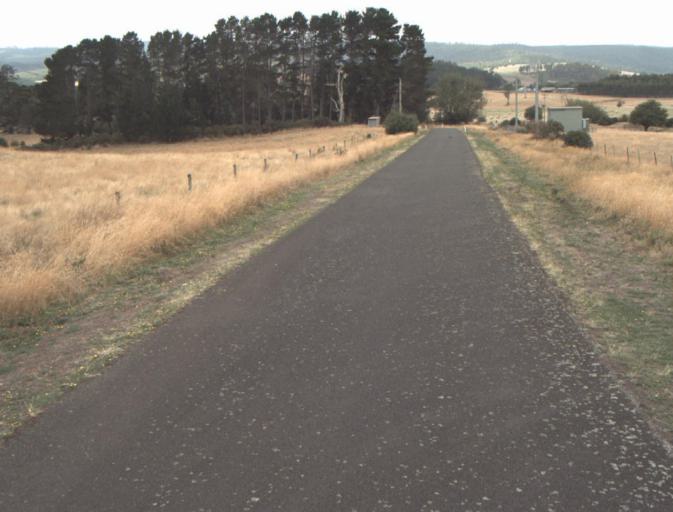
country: AU
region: Tasmania
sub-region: Northern Midlands
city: Evandale
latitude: -41.5070
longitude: 147.4811
